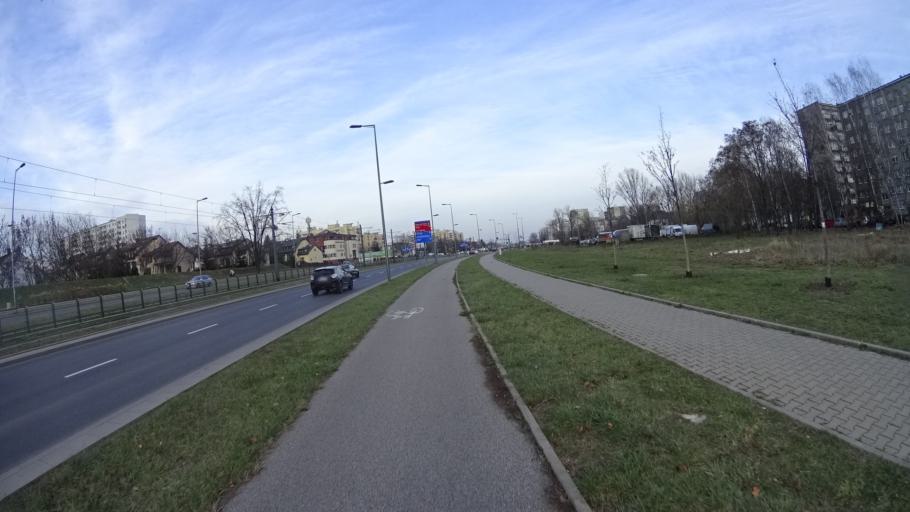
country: PL
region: Masovian Voivodeship
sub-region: Warszawa
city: Bemowo
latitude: 52.2504
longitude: 20.9117
